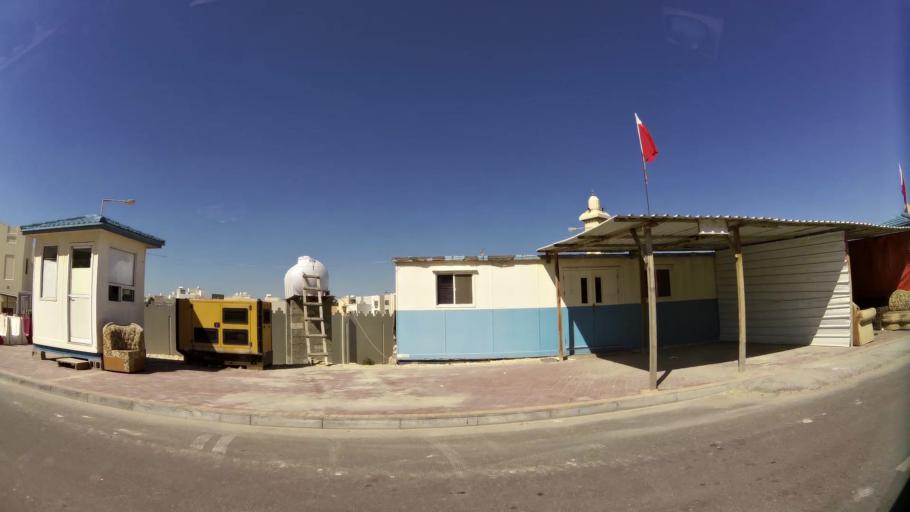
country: BH
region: Muharraq
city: Al Muharraq
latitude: 26.2487
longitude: 50.6311
